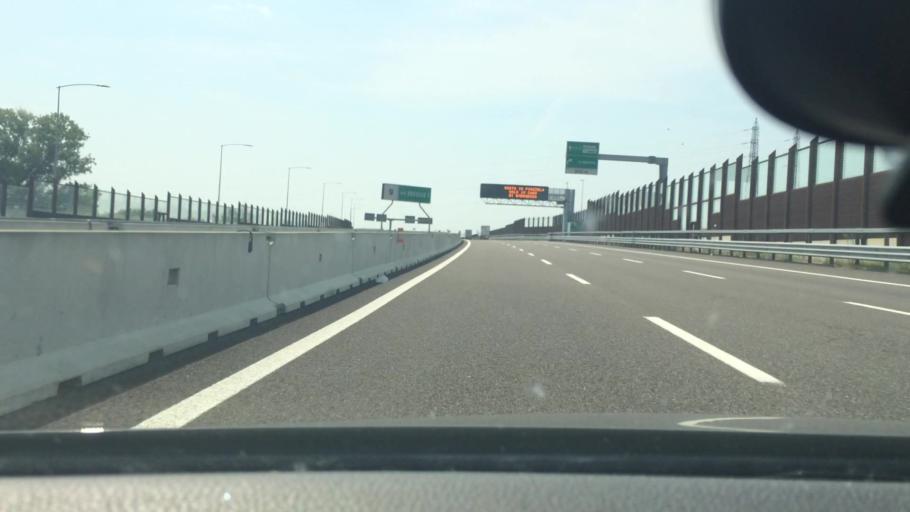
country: IT
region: Lombardy
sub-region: Citta metropolitana di Milano
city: Pozzuolo Martesana
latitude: 45.5099
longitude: 9.4408
